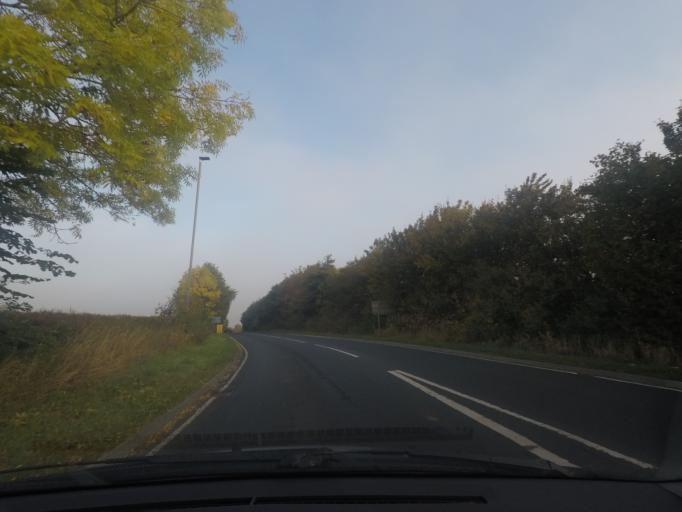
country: GB
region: England
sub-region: City and Borough of Leeds
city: Walton
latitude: 54.0027
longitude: -1.3040
